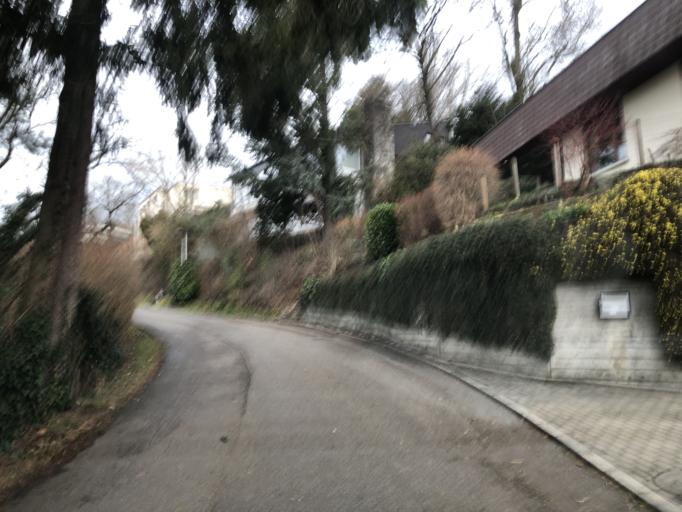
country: CH
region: Aargau
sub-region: Bezirk Baden
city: Obersiggenthal
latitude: 47.4904
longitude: 8.2954
